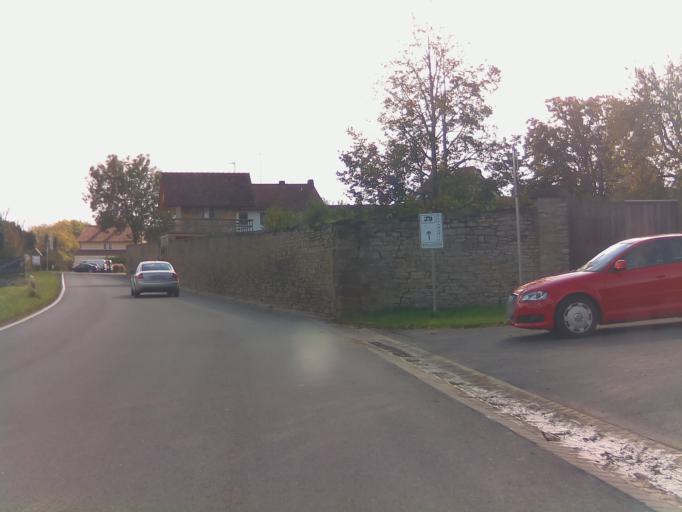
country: DE
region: Bavaria
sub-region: Regierungsbezirk Unterfranken
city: Mainstockheim
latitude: 49.7787
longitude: 10.1514
